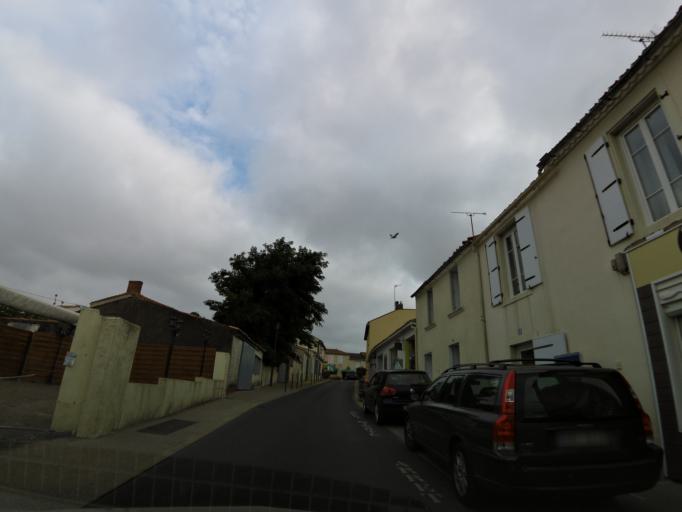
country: FR
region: Pays de la Loire
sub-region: Departement de la Vendee
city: Longeville-sur-Mer
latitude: 46.4241
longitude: -1.4909
